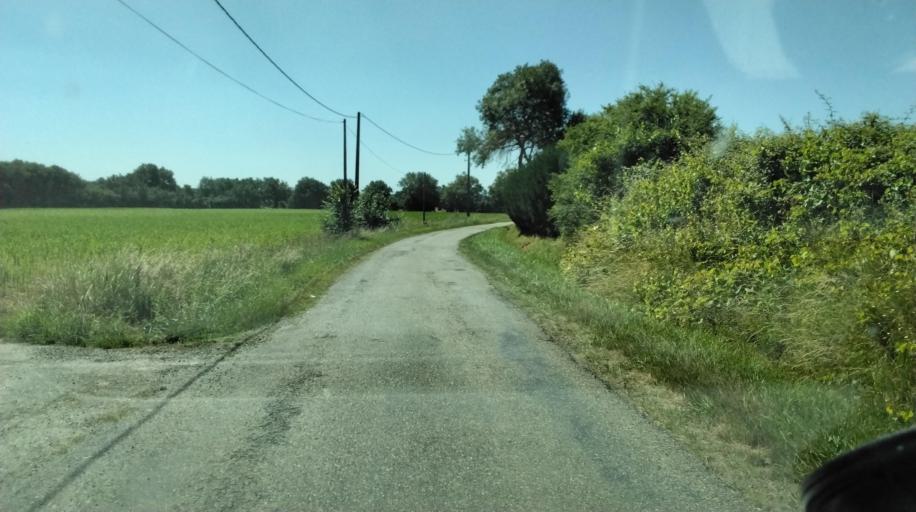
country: FR
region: Midi-Pyrenees
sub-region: Departement de la Haute-Garonne
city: Sainte-Foy-de-Peyrolieres
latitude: 43.4866
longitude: 1.1495
